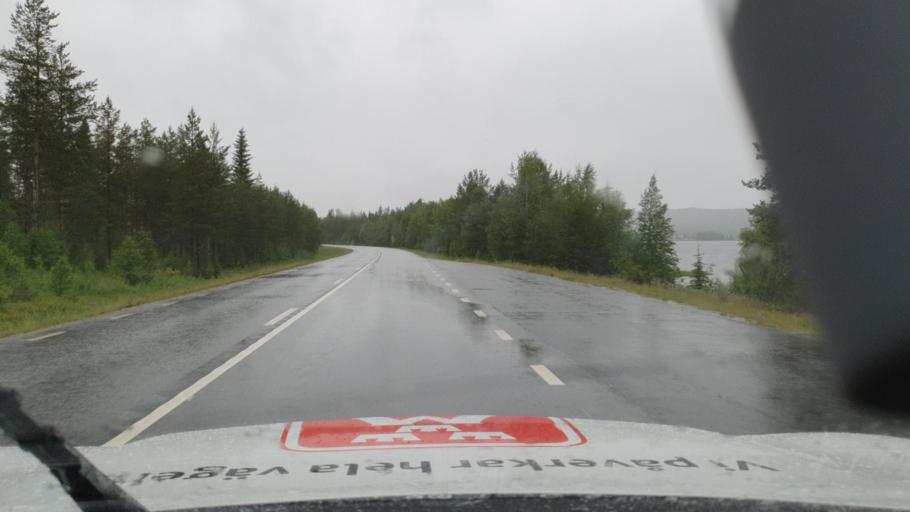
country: SE
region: Vaesterbotten
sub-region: Asele Kommun
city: Insjon
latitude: 64.1897
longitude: 17.7780
